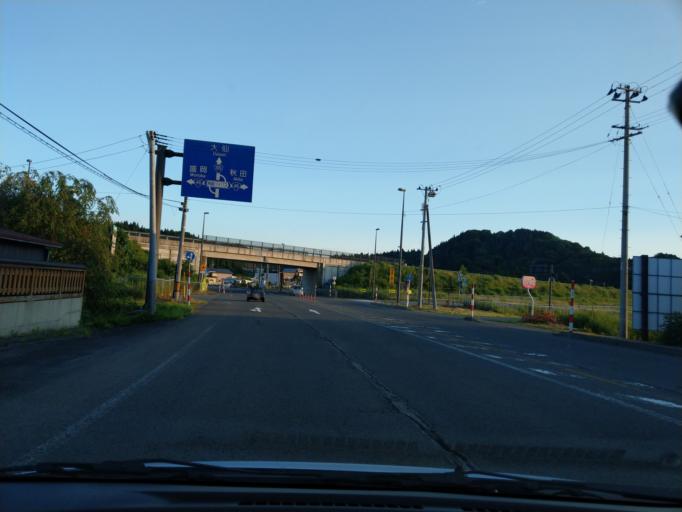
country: JP
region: Akita
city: Kakunodatemachi
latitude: 39.6126
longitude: 140.5700
